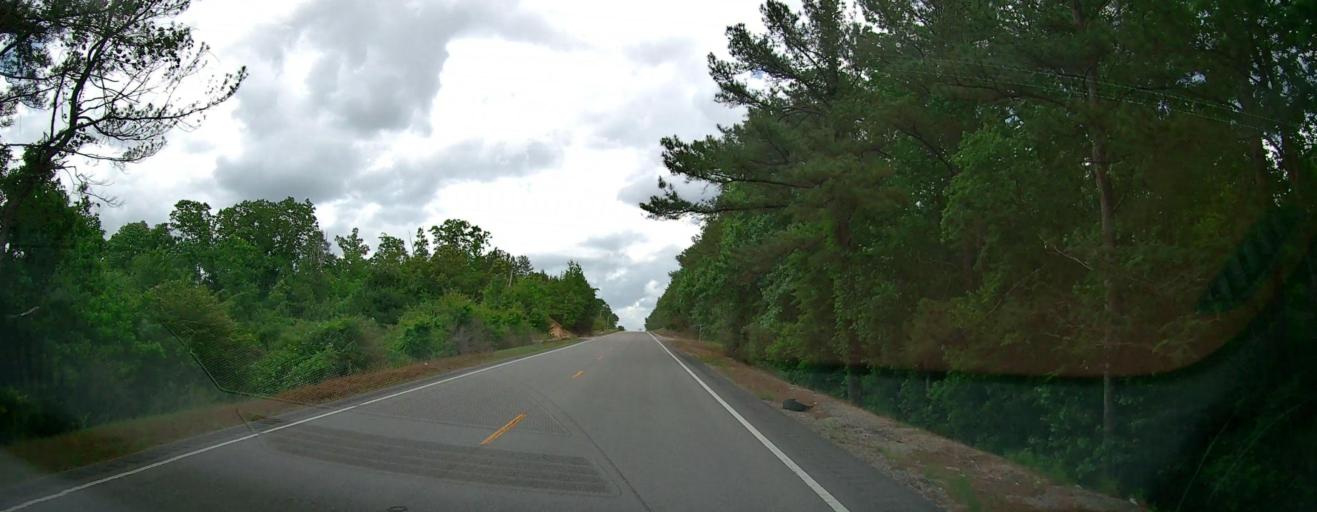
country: US
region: Alabama
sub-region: Marion County
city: Hamilton
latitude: 34.1301
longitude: -88.0273
